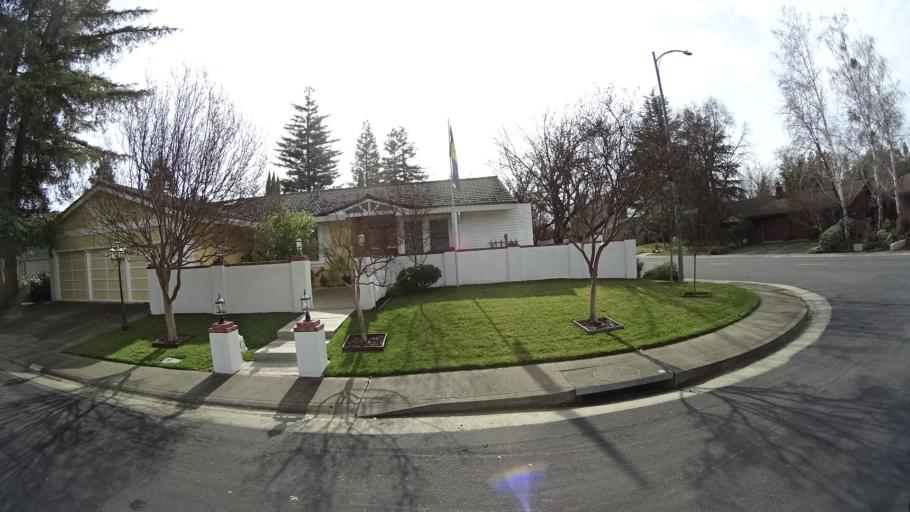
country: US
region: California
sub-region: Yolo County
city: Davis
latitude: 38.5416
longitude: -121.6993
